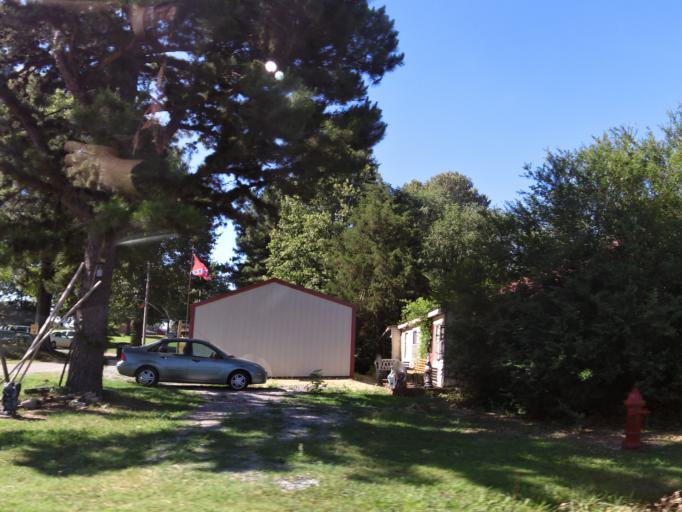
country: US
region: Arkansas
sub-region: Clay County
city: Piggott
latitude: 36.4292
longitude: -90.2728
